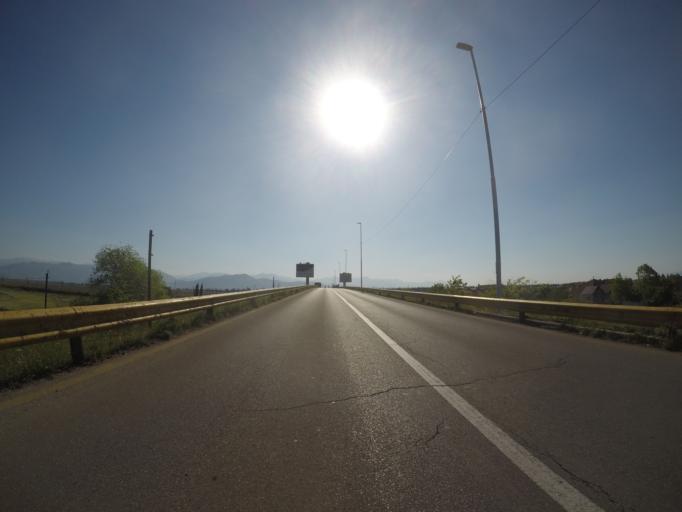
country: ME
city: Mojanovici
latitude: 42.3661
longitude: 19.2330
